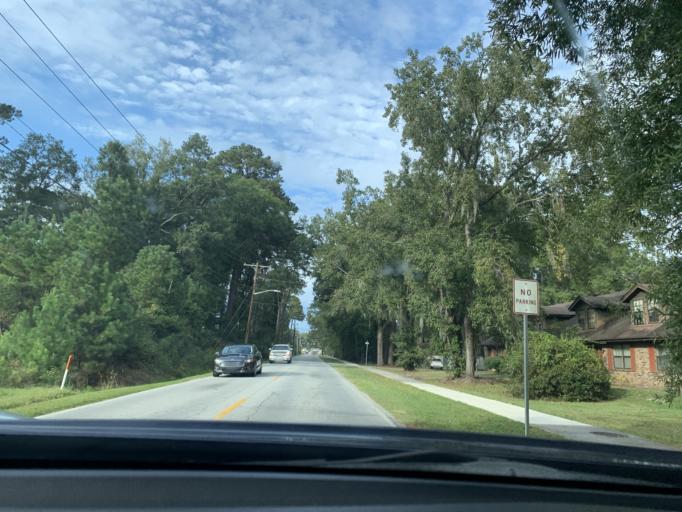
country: US
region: Georgia
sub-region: Chatham County
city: Pooler
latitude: 32.1115
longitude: -81.2503
